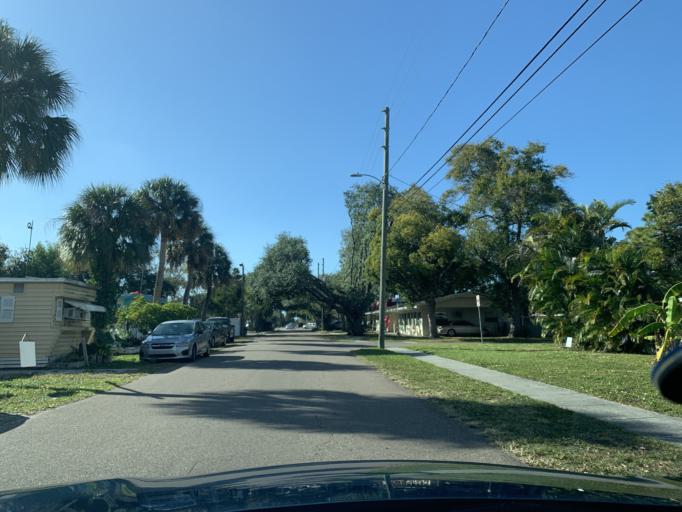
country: US
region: Florida
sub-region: Pinellas County
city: Largo
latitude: 27.9241
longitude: -82.7949
